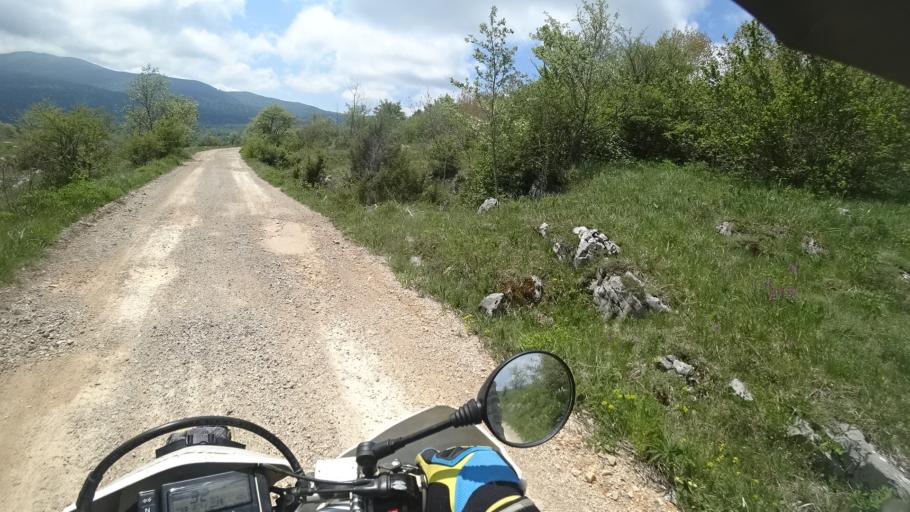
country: HR
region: Zadarska
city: Gracac
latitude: 44.5071
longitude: 15.8862
